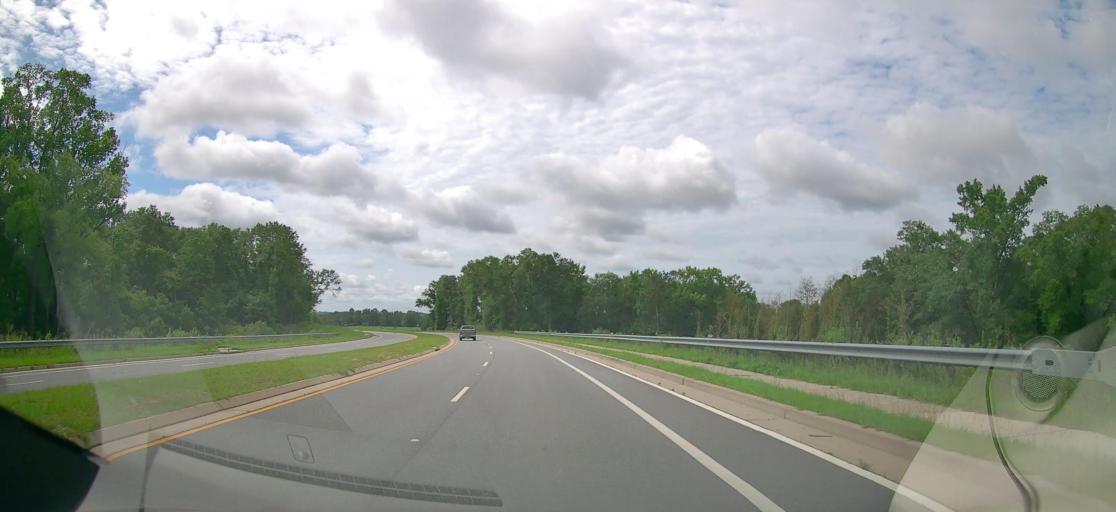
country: US
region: Georgia
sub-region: Houston County
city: Centerville
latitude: 32.7015
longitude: -83.6947
